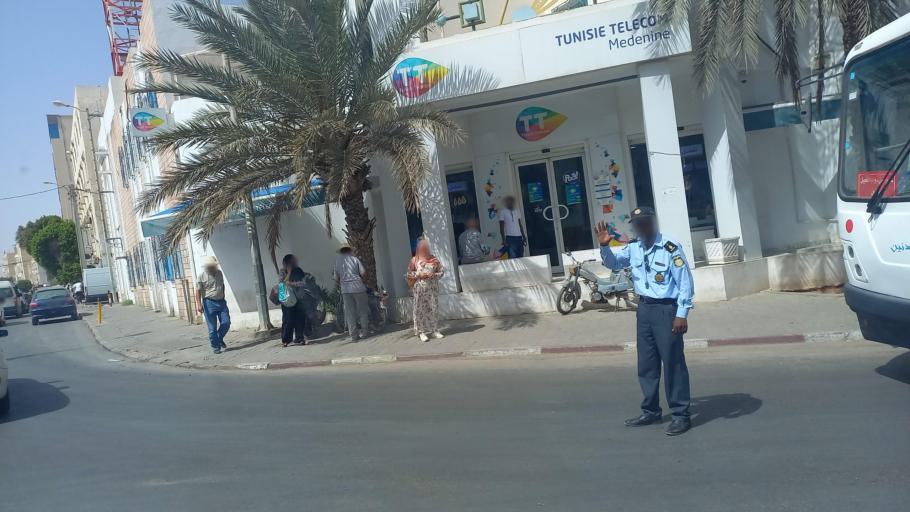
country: TN
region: Madanin
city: Medenine
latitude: 33.3435
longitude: 10.4910
